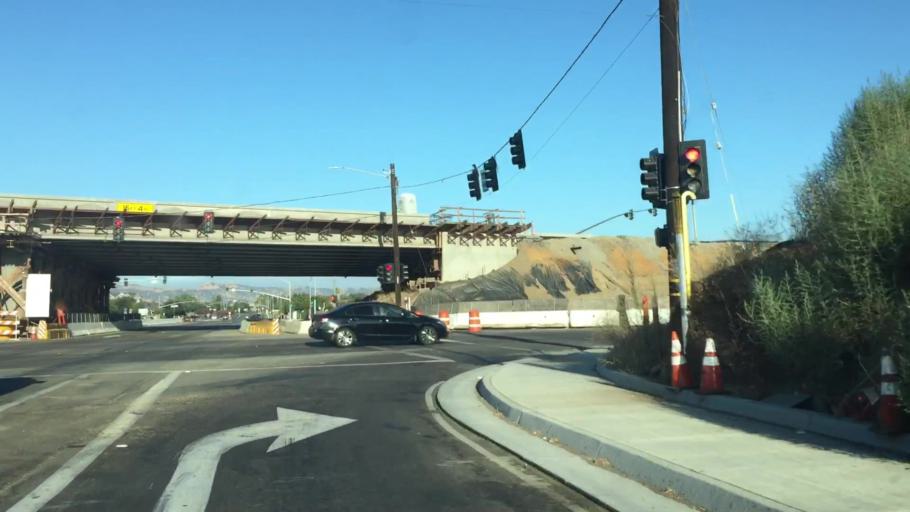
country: US
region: California
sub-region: Contra Costa County
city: Brentwood
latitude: 37.9256
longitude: -121.7325
